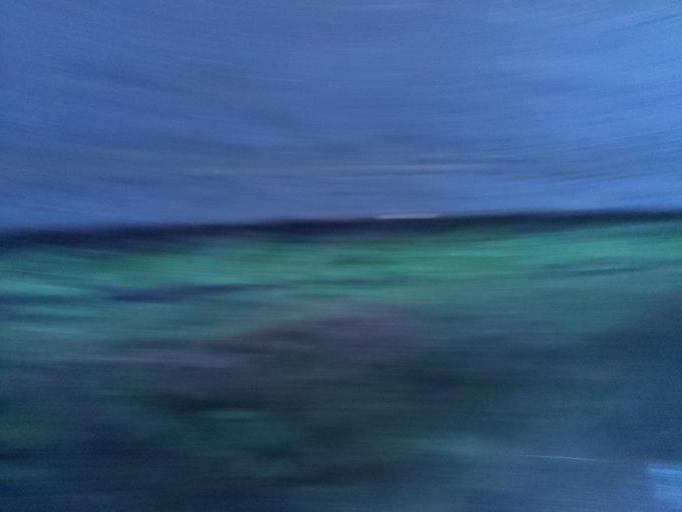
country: GB
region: England
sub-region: Devon
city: Yealmpton
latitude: 50.3371
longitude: -4.0148
